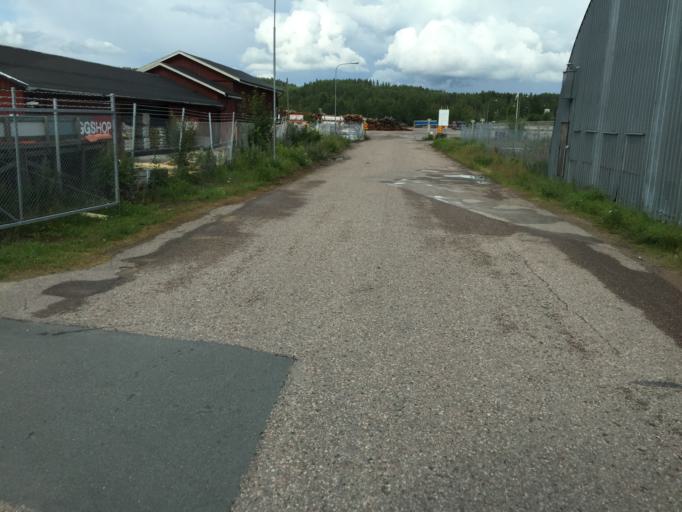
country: SE
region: Dalarna
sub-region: Vansbro Kommun
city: Vansbro
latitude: 60.5105
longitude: 14.2320
